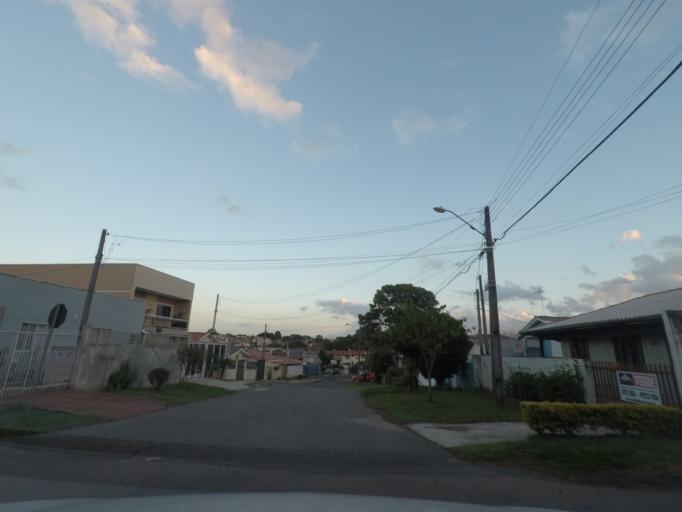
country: BR
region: Parana
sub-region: Sao Jose Dos Pinhais
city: Sao Jose dos Pinhais
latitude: -25.5022
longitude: -49.2607
